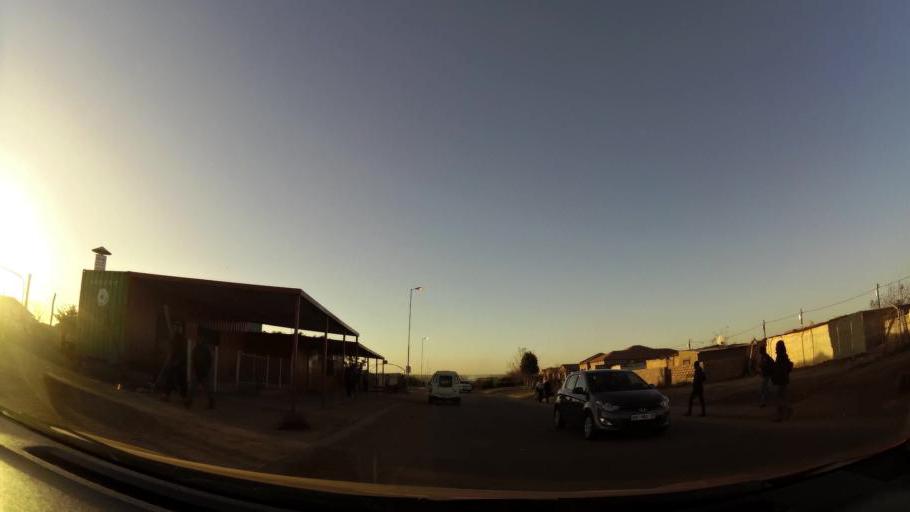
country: ZA
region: North-West
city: Ga-Rankuwa
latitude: -25.5996
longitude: 28.0853
